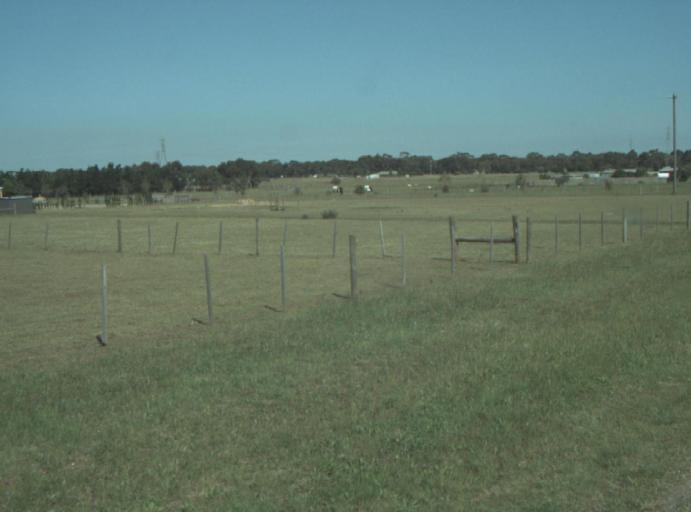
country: AU
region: Victoria
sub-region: Greater Geelong
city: Lara
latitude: -38.0219
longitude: 144.3572
